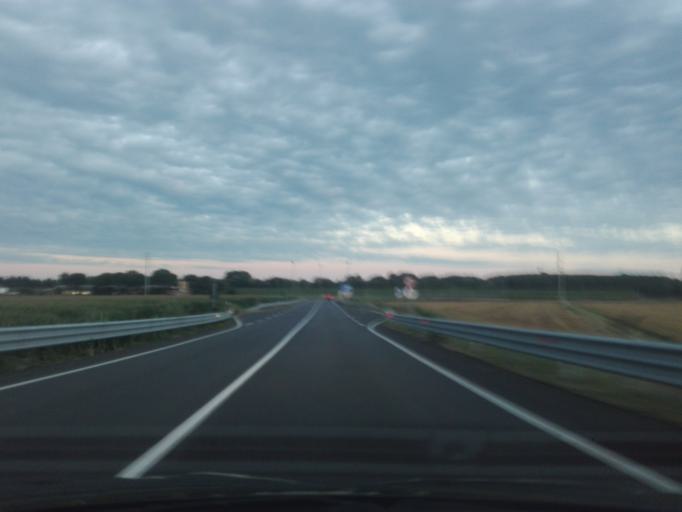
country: IT
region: Veneto
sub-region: Provincia di Rovigo
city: Santa Maria Maddalena
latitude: 44.9015
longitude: 11.6298
